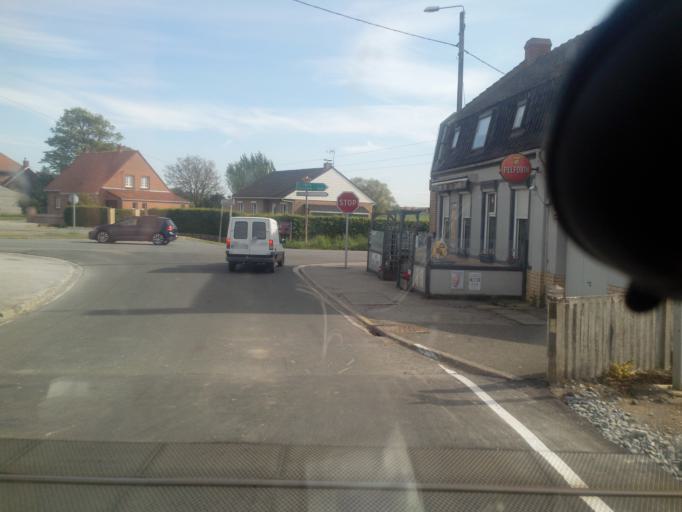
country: FR
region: Nord-Pas-de-Calais
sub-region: Departement du Nord
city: Blaringhem
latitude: 50.7308
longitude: 2.4085
